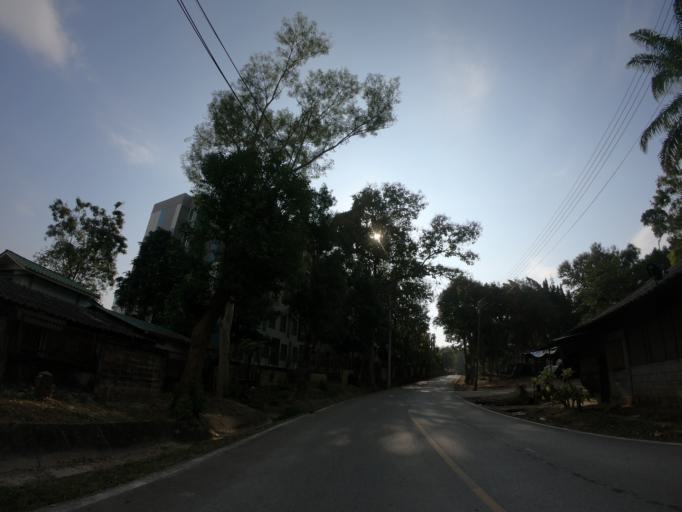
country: TH
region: Chiang Mai
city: Chiang Mai
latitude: 18.7917
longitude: 98.9489
